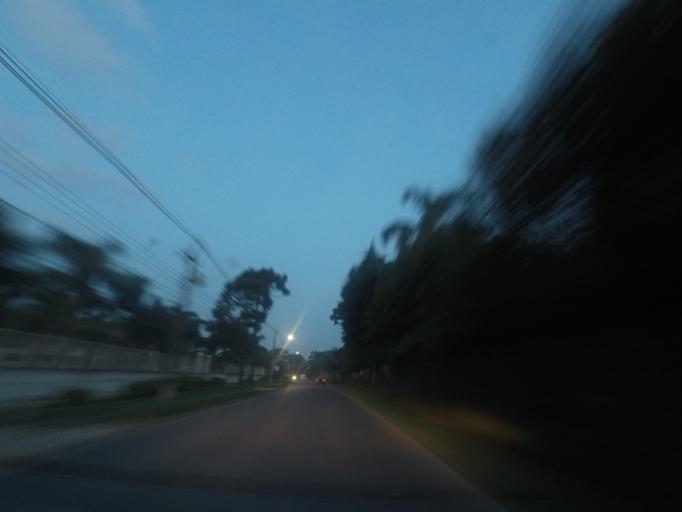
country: BR
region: Parana
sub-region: Pinhais
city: Pinhais
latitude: -25.4622
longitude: -49.1538
